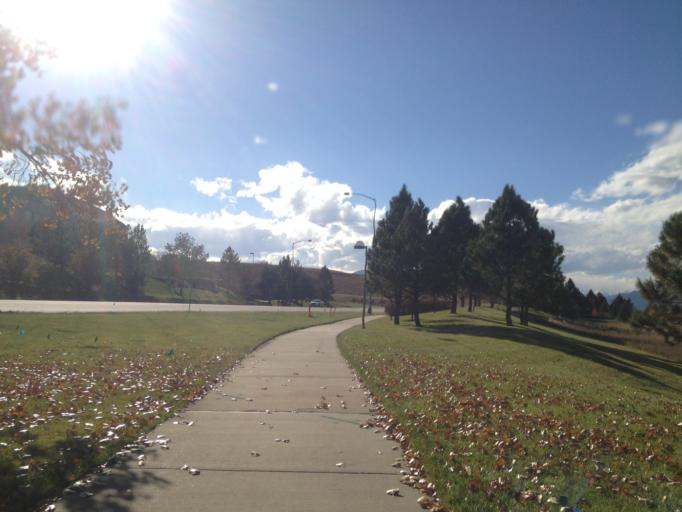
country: US
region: Colorado
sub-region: Broomfield County
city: Broomfield
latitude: 39.9168
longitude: -105.1204
